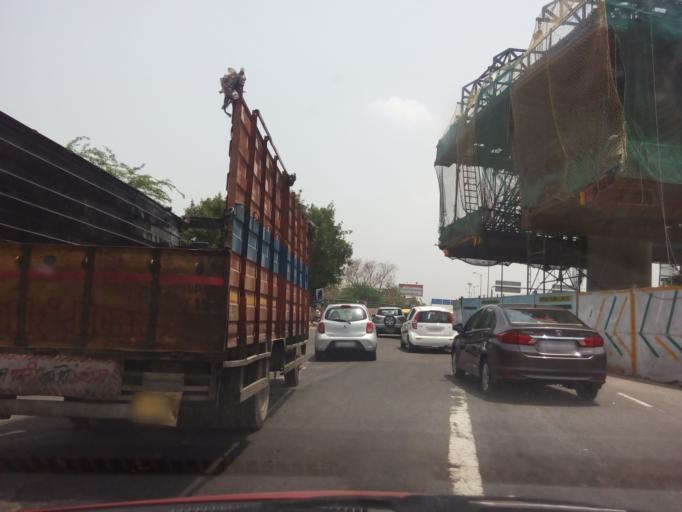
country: IN
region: NCT
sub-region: North West Delhi
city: Pitampura
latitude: 28.6333
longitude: 77.1317
